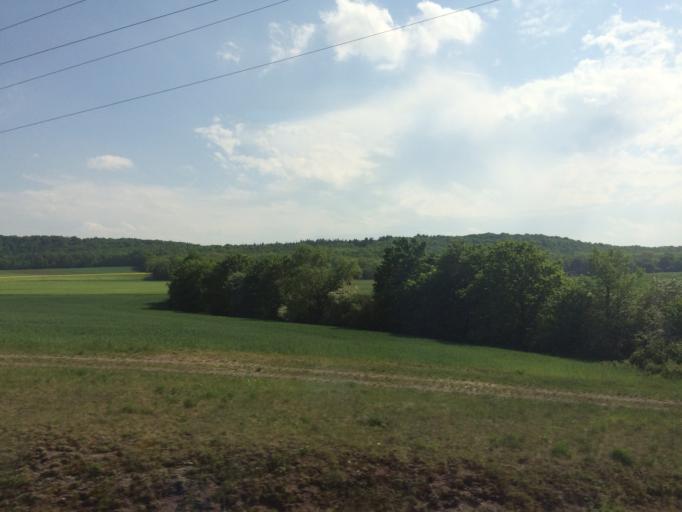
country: DE
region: Bavaria
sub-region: Regierungsbezirk Mittelfranken
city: Scheinfeld
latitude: 49.6416
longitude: 10.4573
